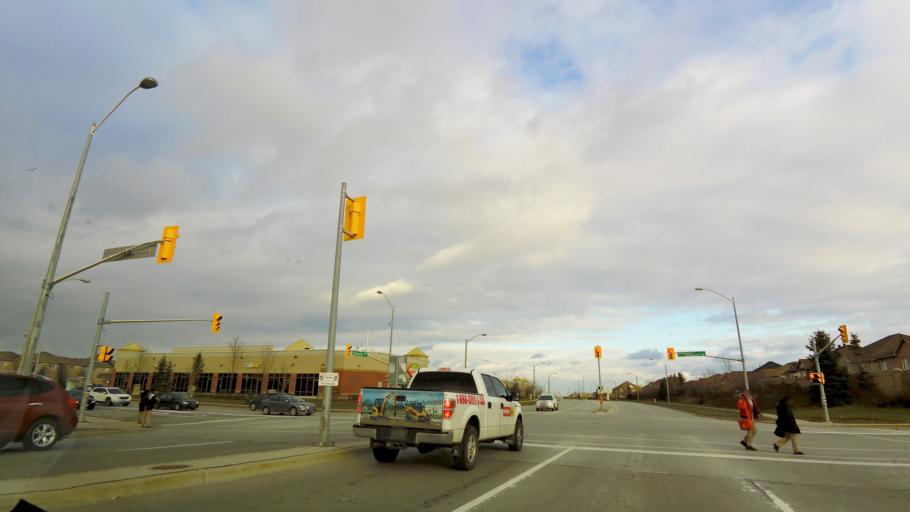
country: CA
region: Ontario
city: Brampton
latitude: 43.7838
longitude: -79.6638
